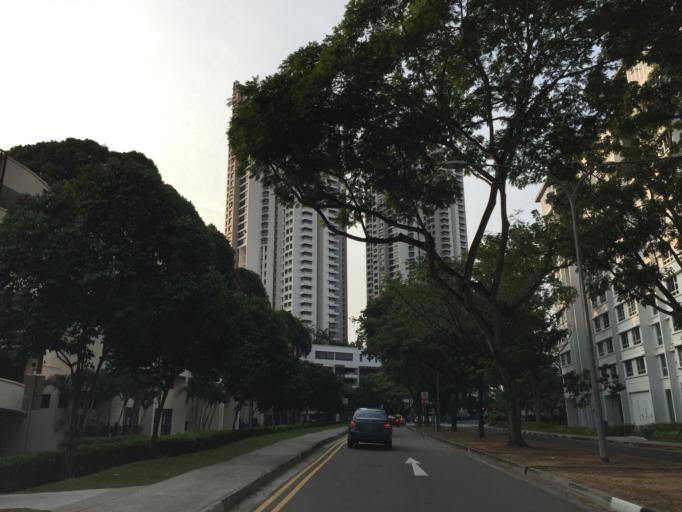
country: SG
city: Singapore
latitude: 1.3021
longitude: 103.7972
